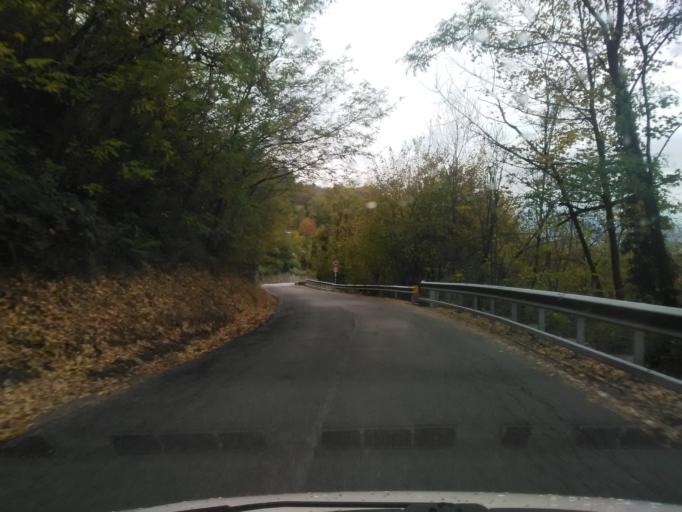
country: IT
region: Piedmont
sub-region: Provincia di Novara
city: Pogno
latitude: 45.7586
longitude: 8.3863
